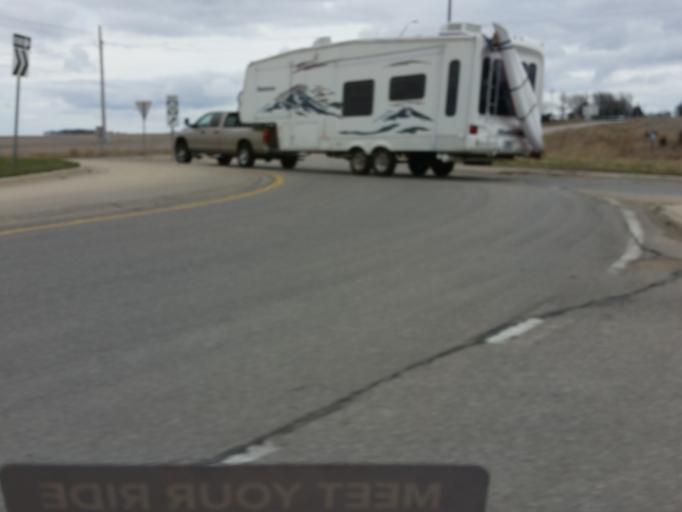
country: US
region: Iowa
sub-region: Black Hawk County
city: Elk Run Heights
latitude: 42.4976
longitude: -92.2198
